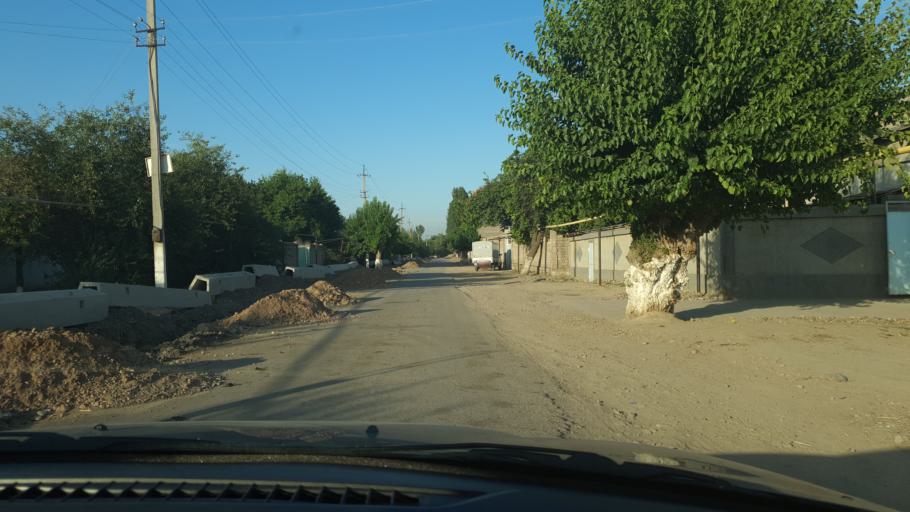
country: UZ
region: Toshkent
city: Tuytepa
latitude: 41.1051
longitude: 69.3914
